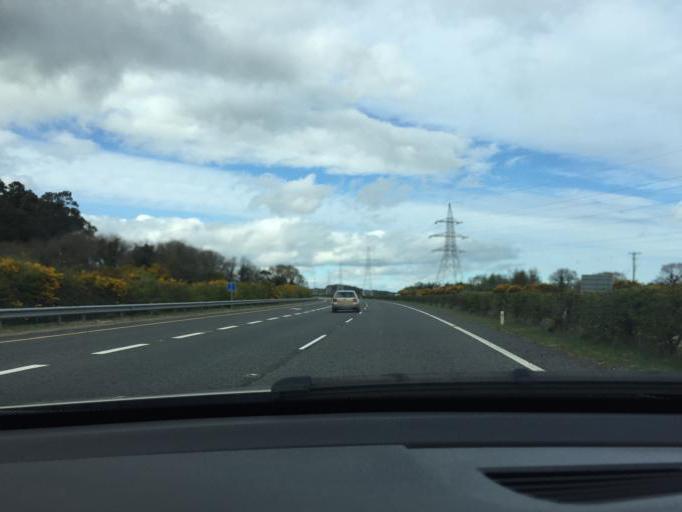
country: IE
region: Leinster
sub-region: Wicklow
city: Ashford
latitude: 53.0377
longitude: -6.0885
